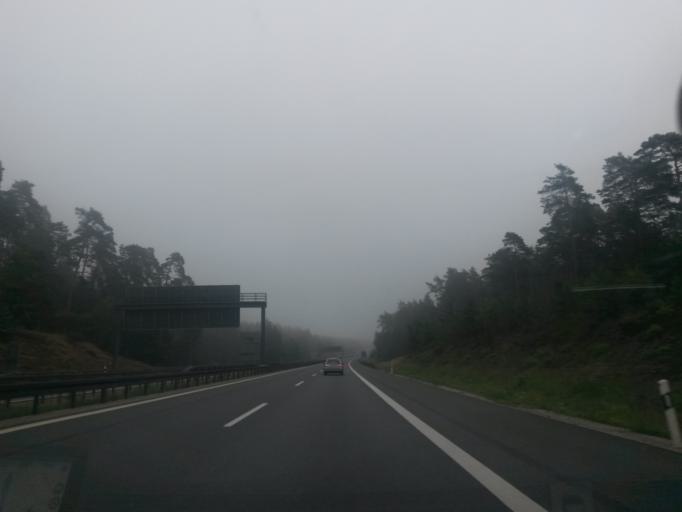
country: DE
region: Bavaria
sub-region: Regierungsbezirk Mittelfranken
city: Winkelhaid
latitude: 49.4078
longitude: 11.3209
